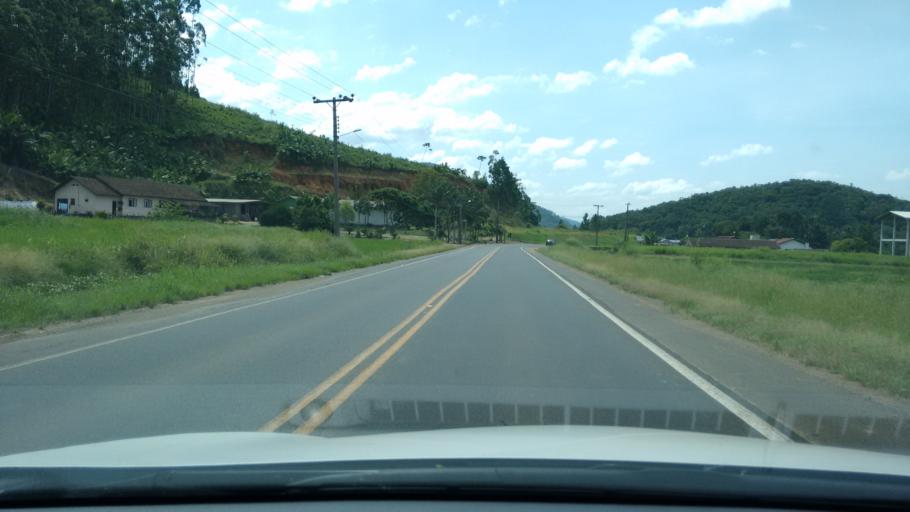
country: BR
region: Santa Catarina
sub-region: Rodeio
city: Gavea
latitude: -26.8881
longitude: -49.3491
